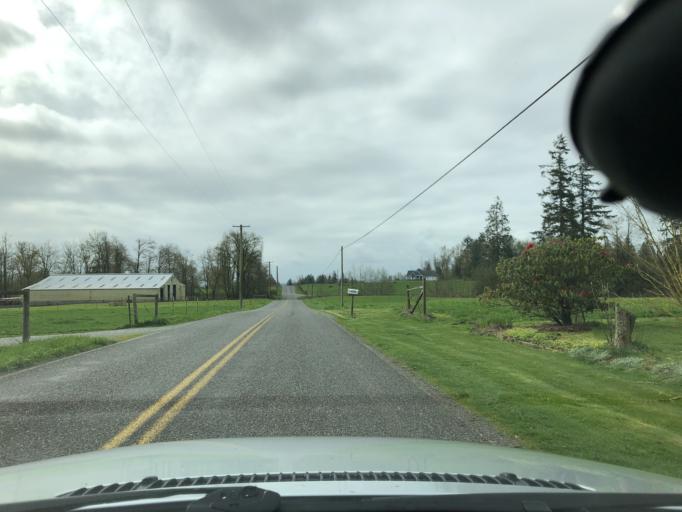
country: US
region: Washington
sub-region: Whatcom County
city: Lynden
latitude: 48.9817
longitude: -122.5522
